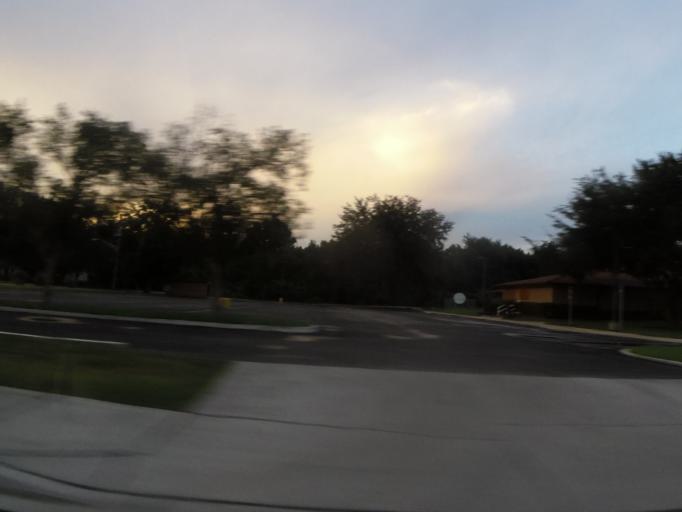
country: US
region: Florida
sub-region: Duval County
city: Jacksonville
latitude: 30.3667
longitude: -81.5717
